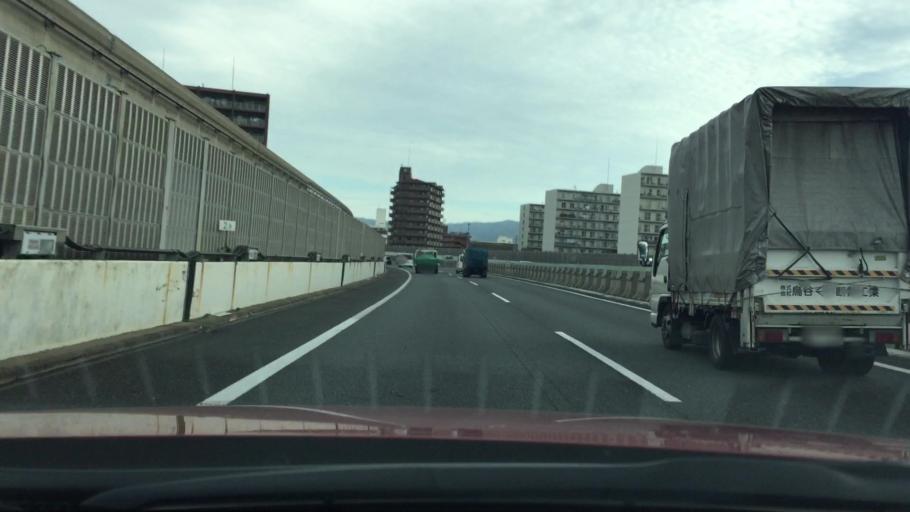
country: JP
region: Osaka
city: Ibaraki
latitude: 34.7976
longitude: 135.5667
